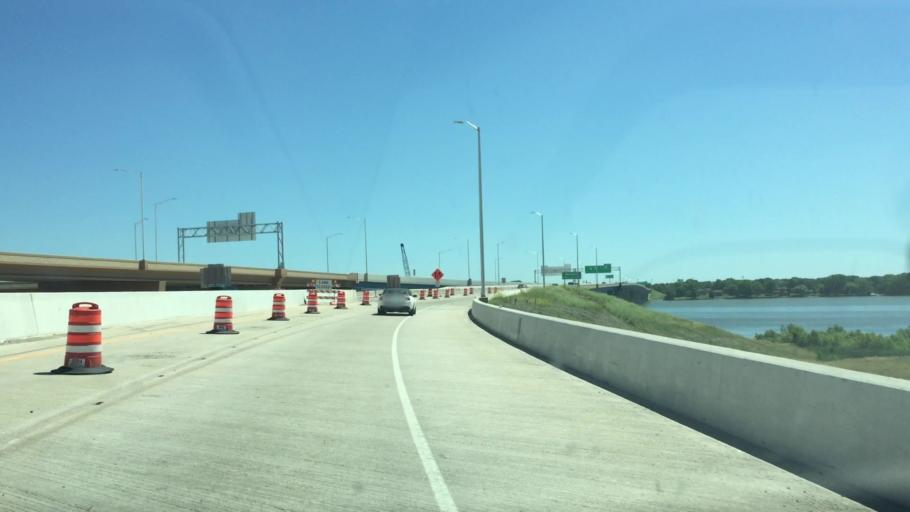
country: US
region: Wisconsin
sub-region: Winnebago County
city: Menasha
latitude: 44.2178
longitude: -88.4702
